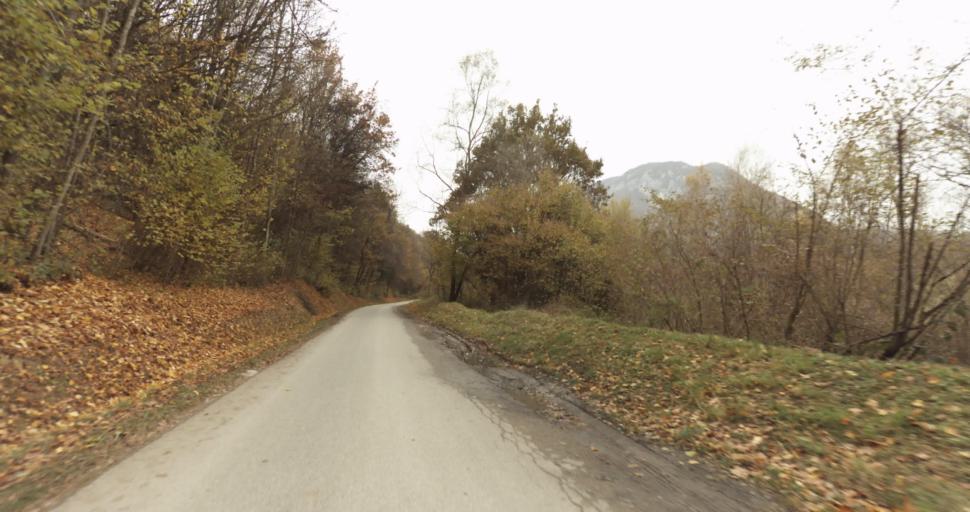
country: FR
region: Rhone-Alpes
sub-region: Departement de la Haute-Savoie
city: Poisy
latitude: 45.9375
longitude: 6.0641
